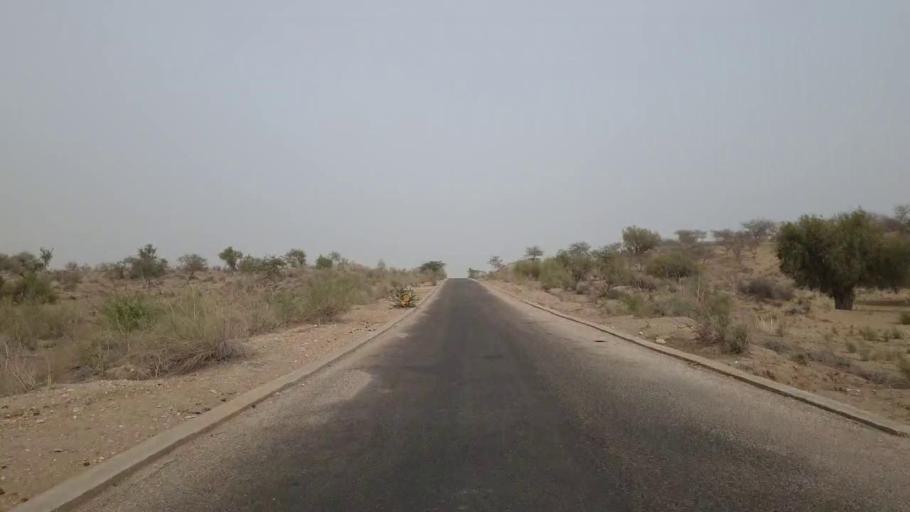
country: PK
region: Sindh
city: Islamkot
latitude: 24.5873
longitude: 70.2929
